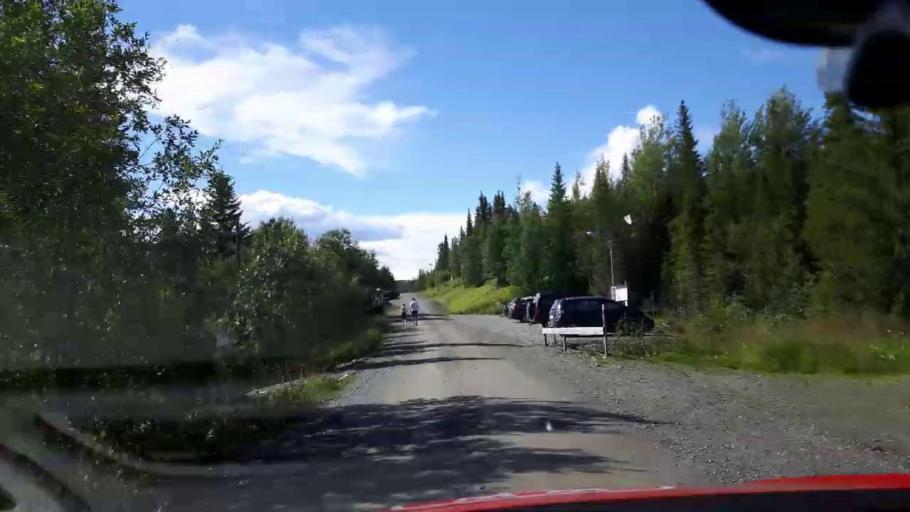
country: SE
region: Jaemtland
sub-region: Are Kommun
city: Are
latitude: 63.2190
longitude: 13.0566
